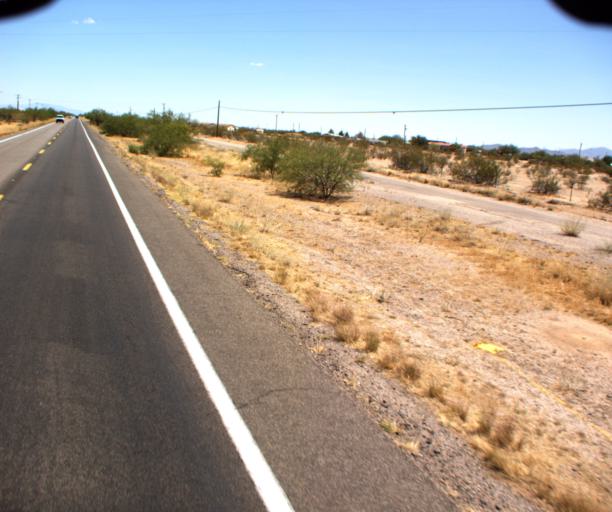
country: US
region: Arizona
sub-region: Pinal County
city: Florence
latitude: 32.9825
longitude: -111.3565
